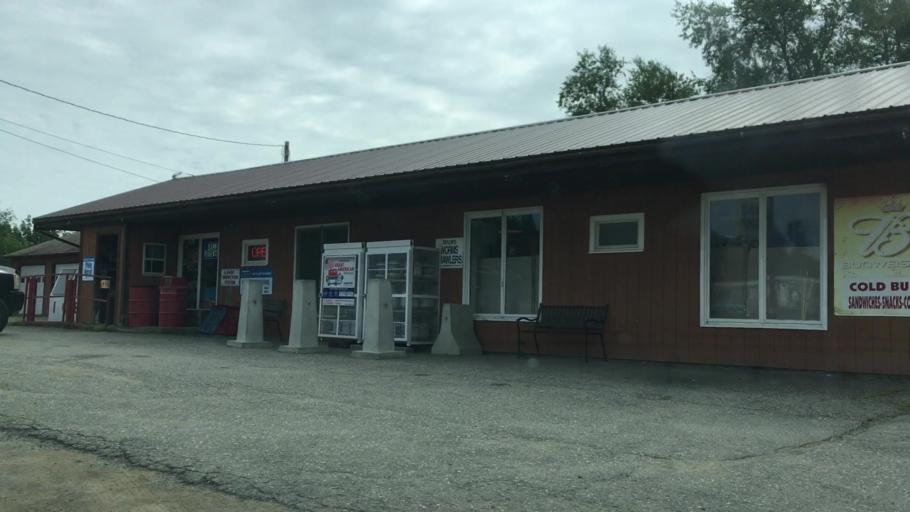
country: US
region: Maine
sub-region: Washington County
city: Calais
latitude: 45.0941
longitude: -67.4682
